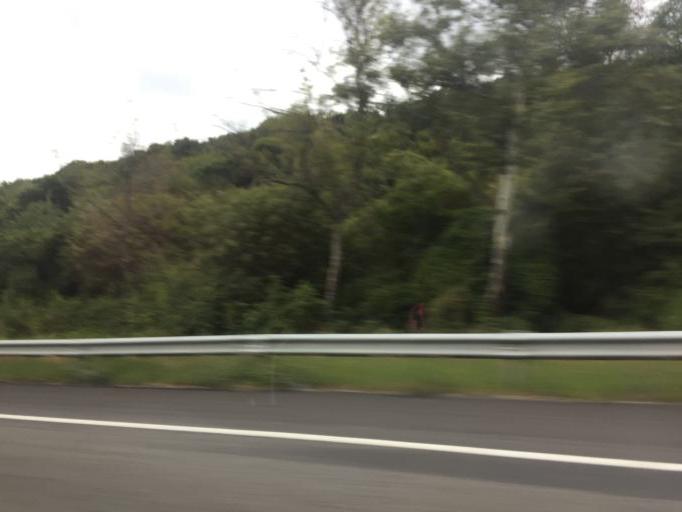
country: MX
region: Jalisco
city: Ocotlan
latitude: 20.4227
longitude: -102.7681
